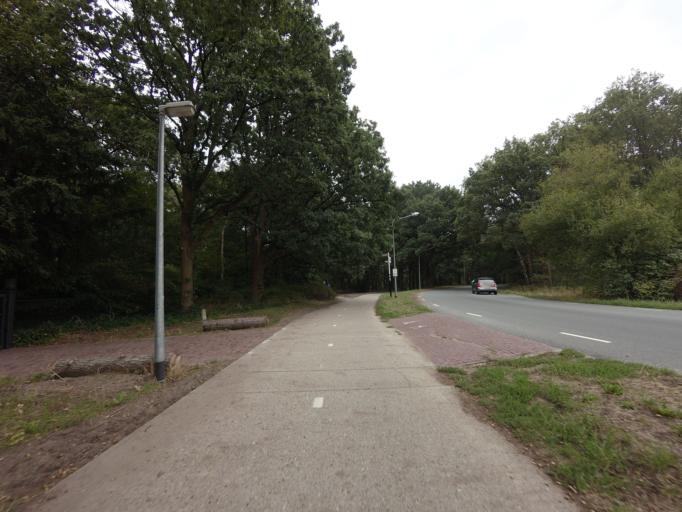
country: NL
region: North Holland
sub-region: Gemeente Wijdemeren
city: Nieuw-Loosdrecht
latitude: 52.1982
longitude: 5.1490
